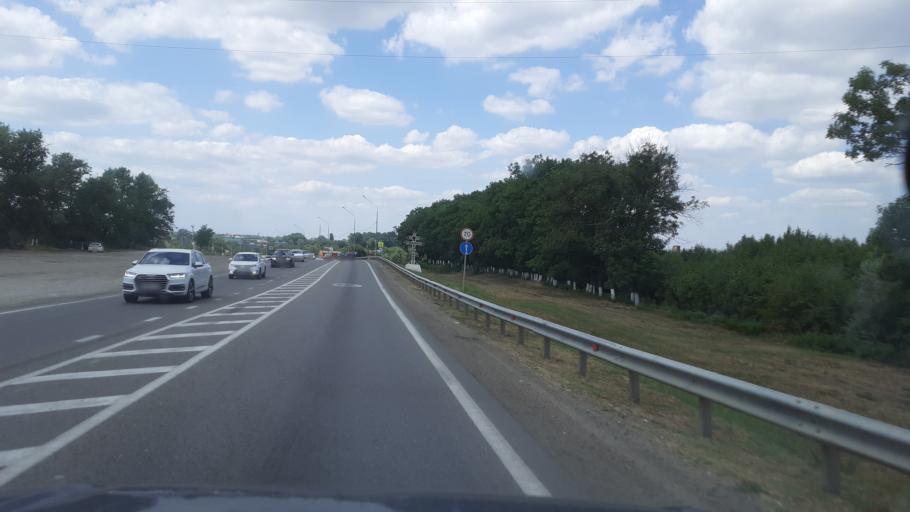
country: RU
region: Krasnodarskiy
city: Il'skiy
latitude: 44.8525
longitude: 38.5953
